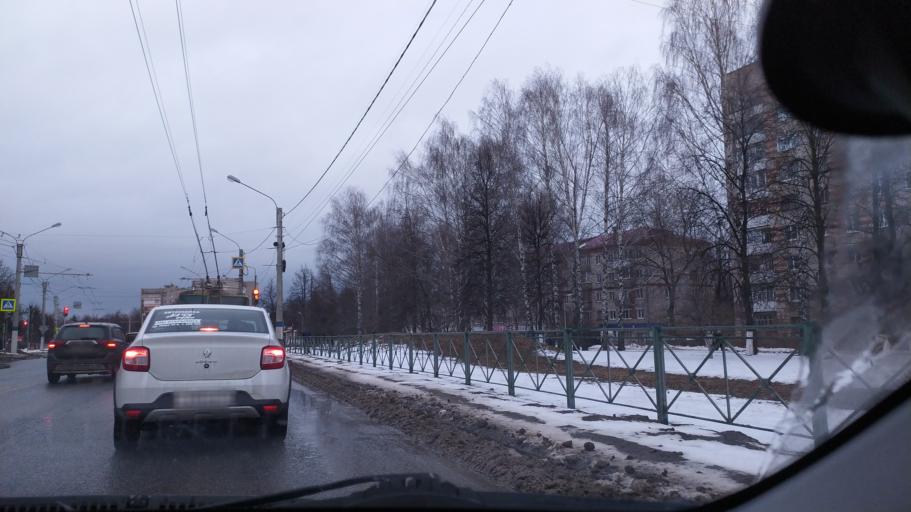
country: RU
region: Chuvashia
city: Novocheboksarsk
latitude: 56.1172
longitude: 47.4920
